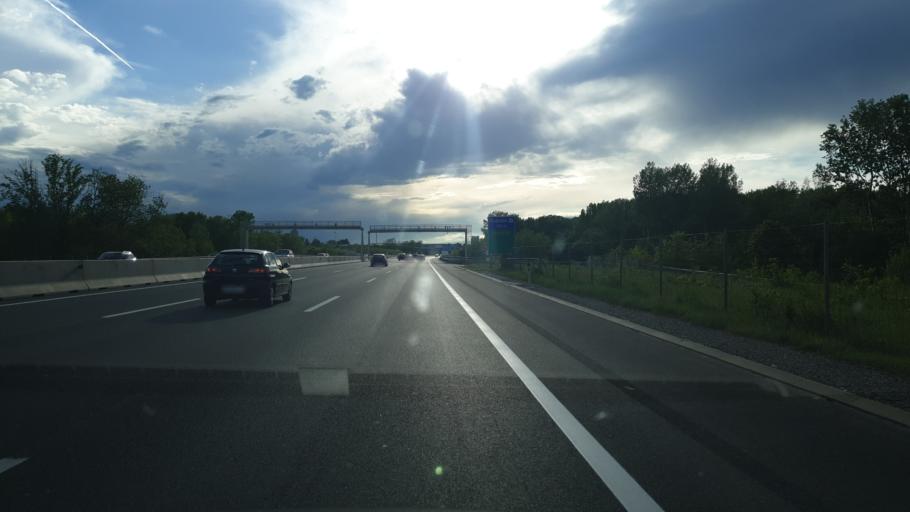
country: AT
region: Lower Austria
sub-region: Politischer Bezirk Wien-Umgebung
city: Fischamend Dorf
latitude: 48.1293
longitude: 16.5616
